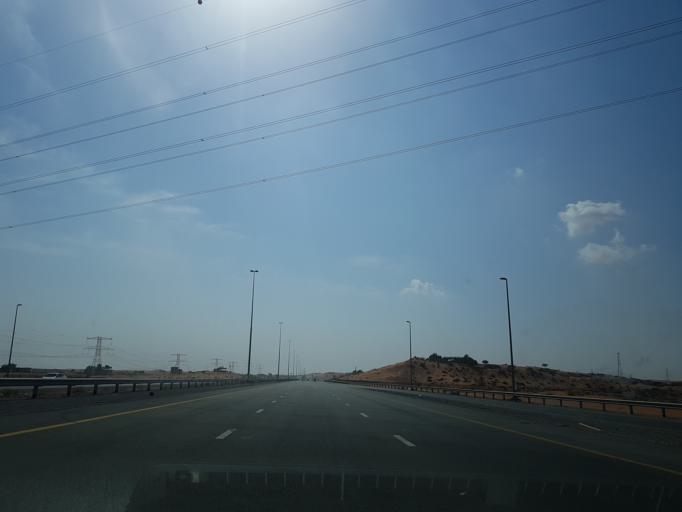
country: AE
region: Ra's al Khaymah
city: Ras al-Khaimah
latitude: 25.6935
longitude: 55.9231
